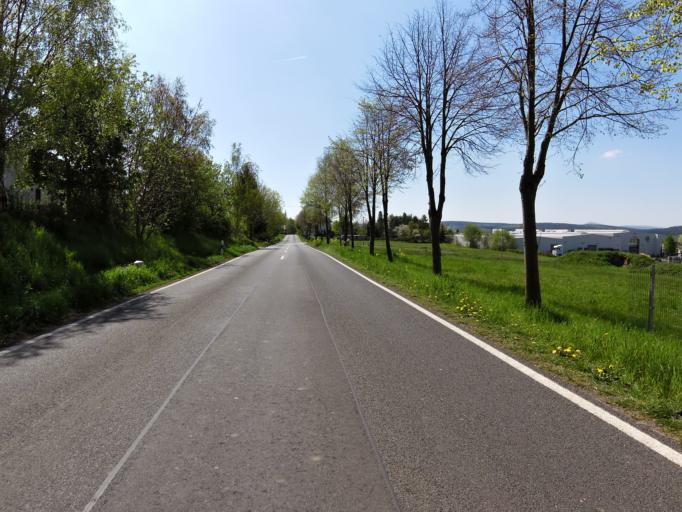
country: DE
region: Thuringia
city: Marksuhl
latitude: 50.9080
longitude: 10.2223
